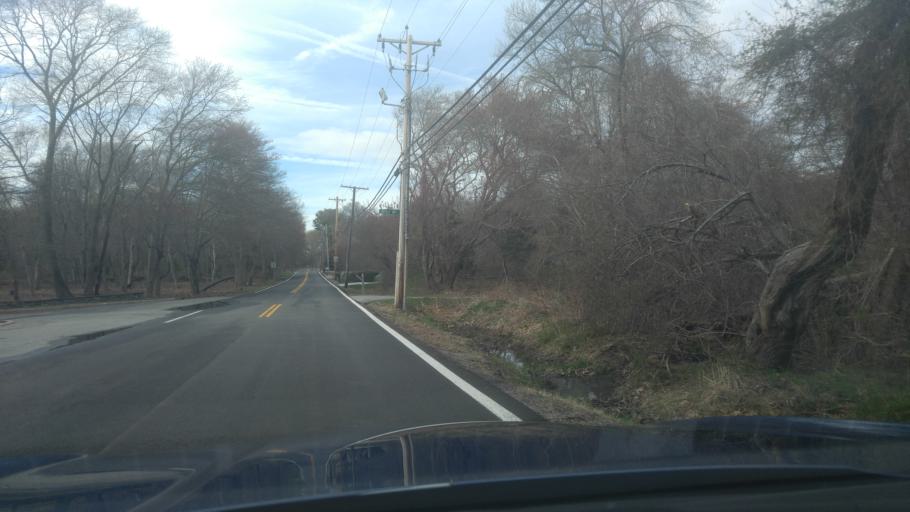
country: US
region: Rhode Island
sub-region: Newport County
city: Jamestown
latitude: 41.5525
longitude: -71.3631
